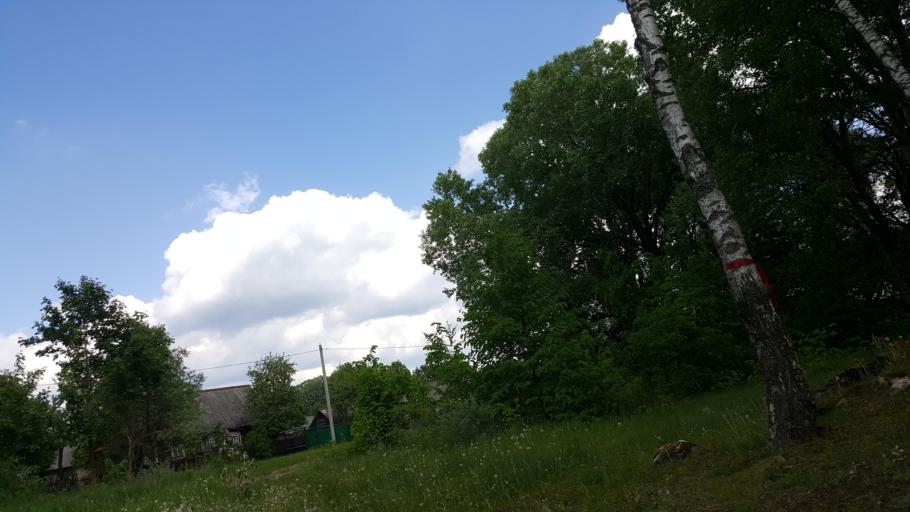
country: BY
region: Brest
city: Kamyanyets
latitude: 52.4782
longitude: 23.9693
